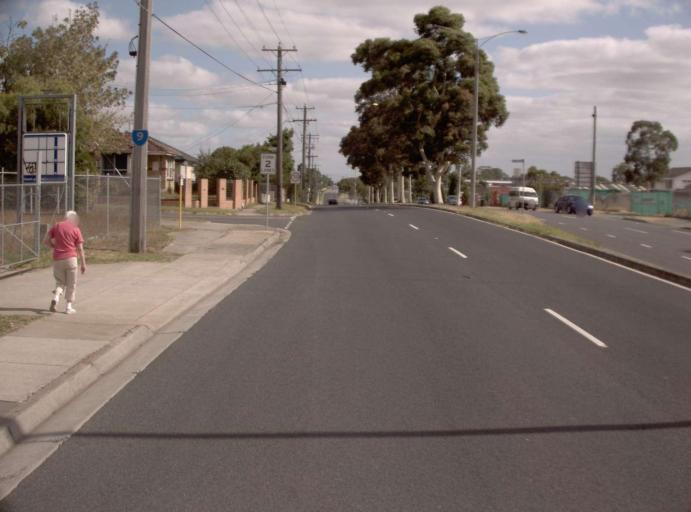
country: AU
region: Victoria
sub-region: Greater Dandenong
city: Dandenong North
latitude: -37.9716
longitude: 145.2235
